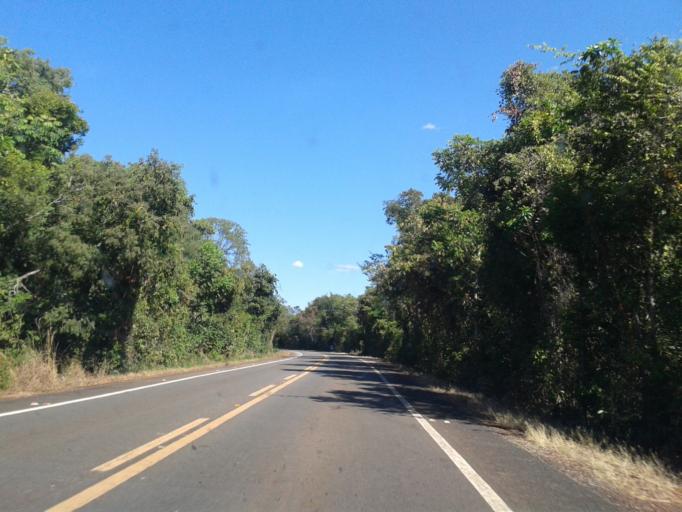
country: BR
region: Goias
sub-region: Sao Miguel Do Araguaia
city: Sao Miguel do Araguaia
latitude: -13.8123
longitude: -50.3430
